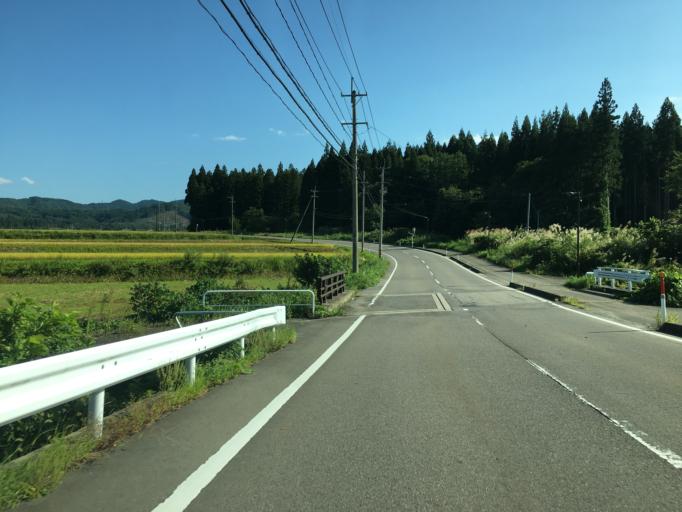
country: JP
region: Fukushima
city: Kitakata
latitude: 37.5950
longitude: 139.6538
